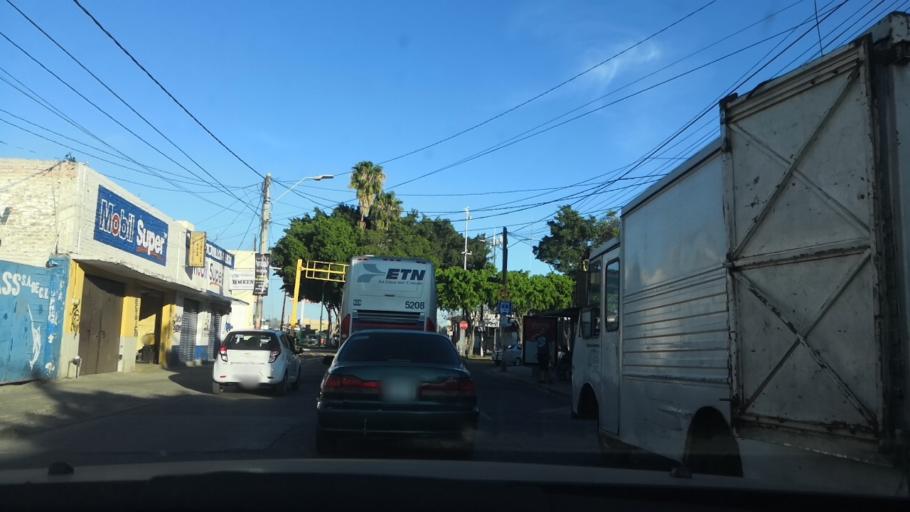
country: MX
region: Guanajuato
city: Leon
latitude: 21.1213
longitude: -101.6573
